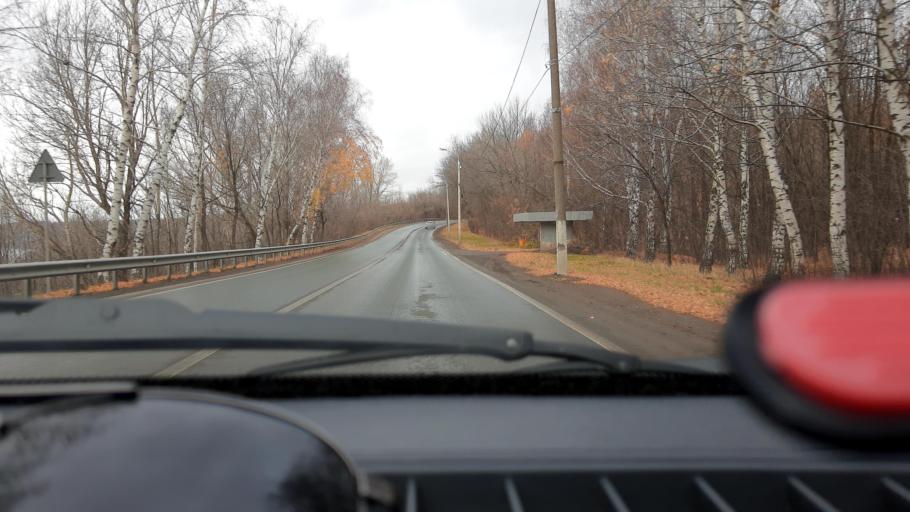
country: RU
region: Bashkortostan
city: Ufa
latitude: 54.8540
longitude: 56.0734
